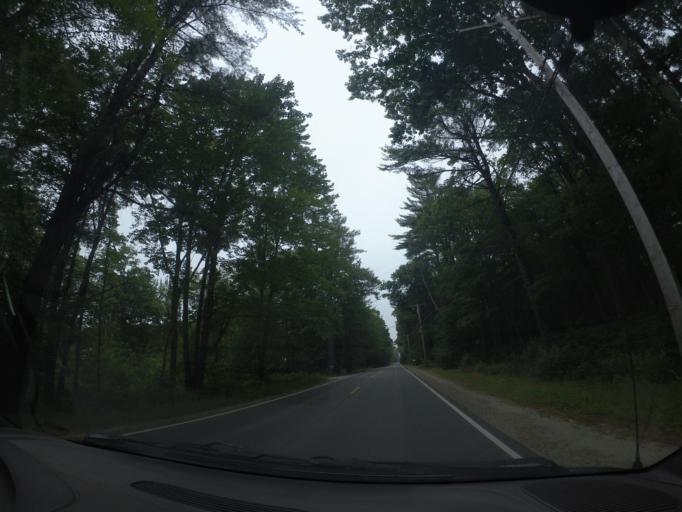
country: US
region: Maine
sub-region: York County
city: Arundel
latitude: 43.3898
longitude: -70.4813
